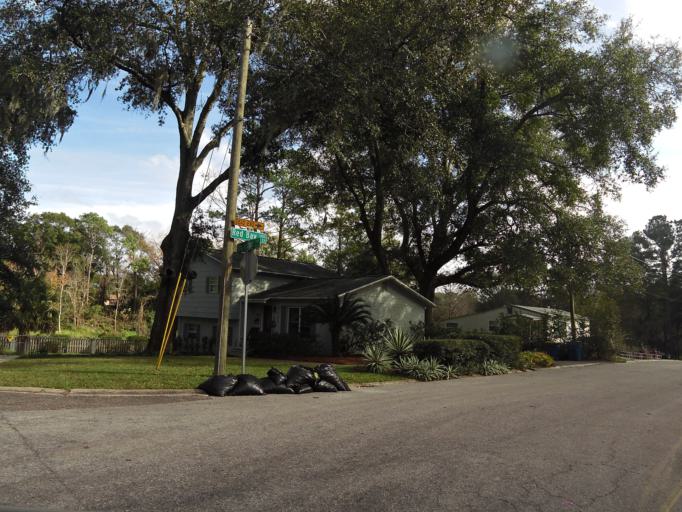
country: US
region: Florida
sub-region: Duval County
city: Jacksonville
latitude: 30.3440
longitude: -81.5824
